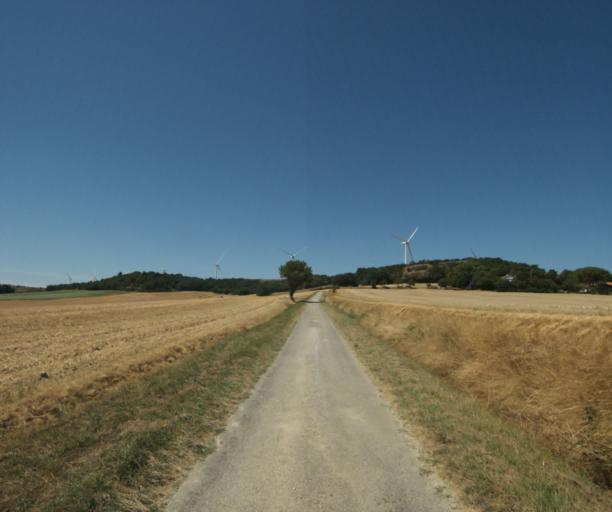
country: FR
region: Midi-Pyrenees
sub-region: Departement de la Haute-Garonne
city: Saint-Felix-Lauragais
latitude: 43.4585
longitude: 1.9256
